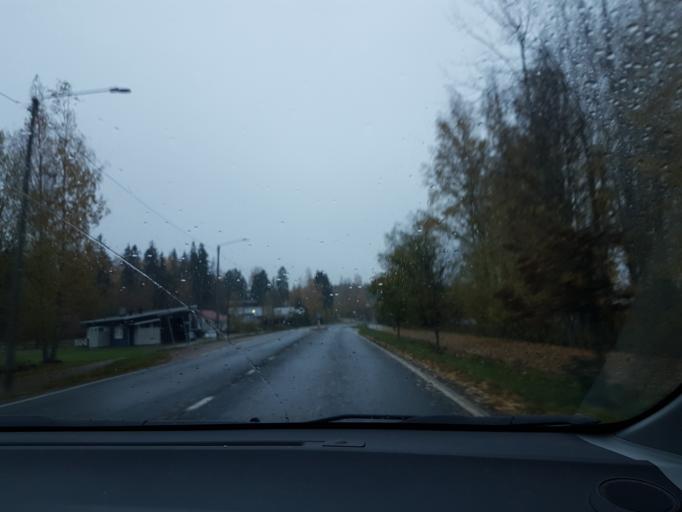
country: FI
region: Uusimaa
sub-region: Helsinki
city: Jaervenpaeae
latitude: 60.5400
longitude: 25.1142
